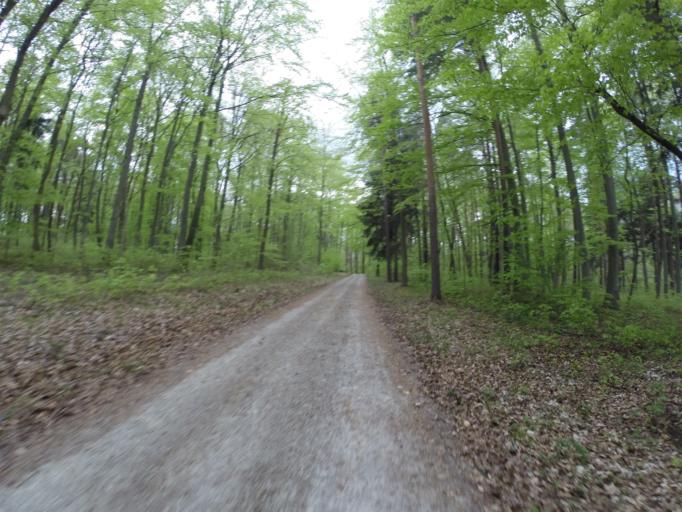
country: DE
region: Thuringia
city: Grosslobichau
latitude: 50.9408
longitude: 11.6628
